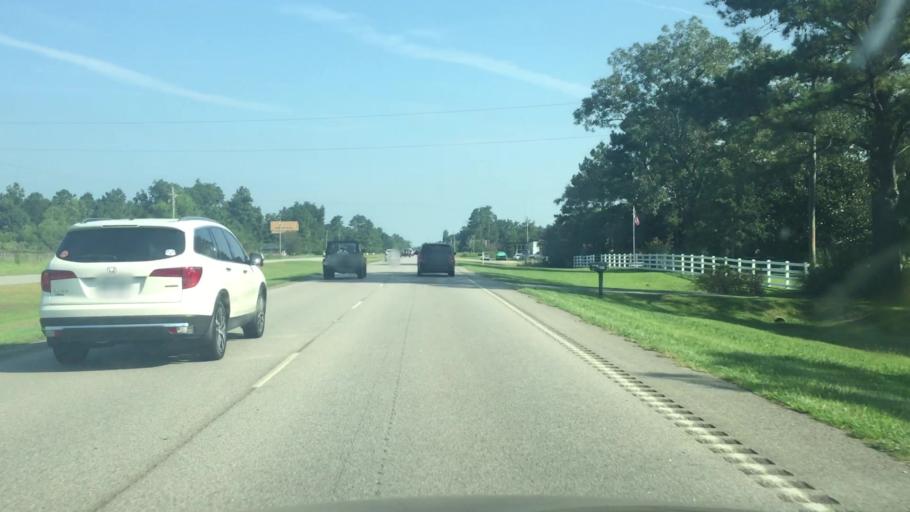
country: US
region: South Carolina
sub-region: Horry County
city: Little River
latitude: 33.9581
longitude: -78.7366
